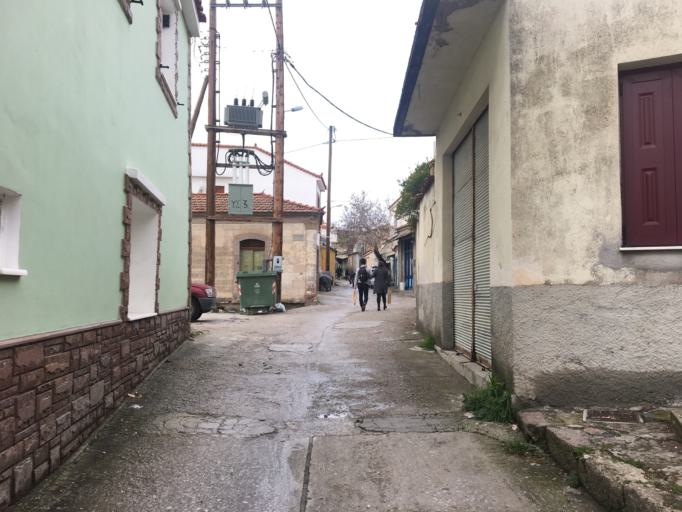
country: GR
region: North Aegean
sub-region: Nomos Lesvou
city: Agia Paraskevi
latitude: 39.2490
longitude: 26.2704
